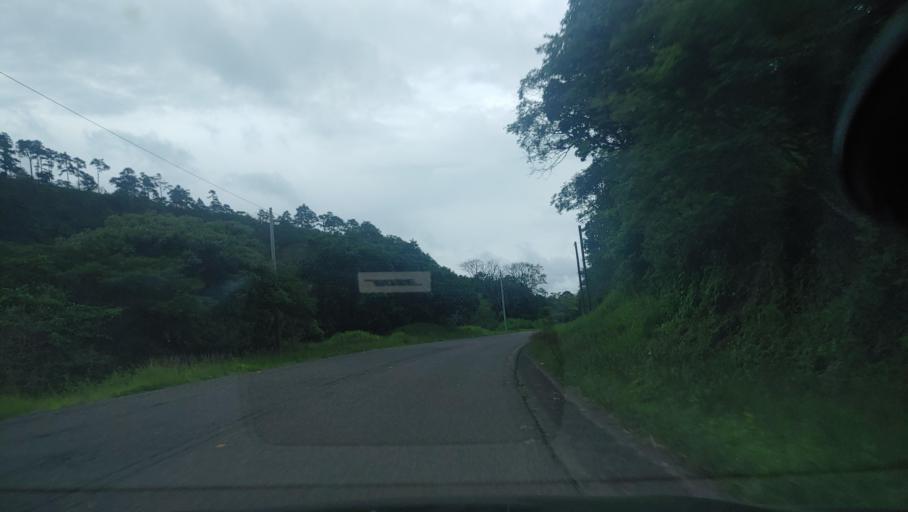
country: HN
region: Choluteca
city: San Marcos de Colon
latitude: 13.3845
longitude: -86.8672
